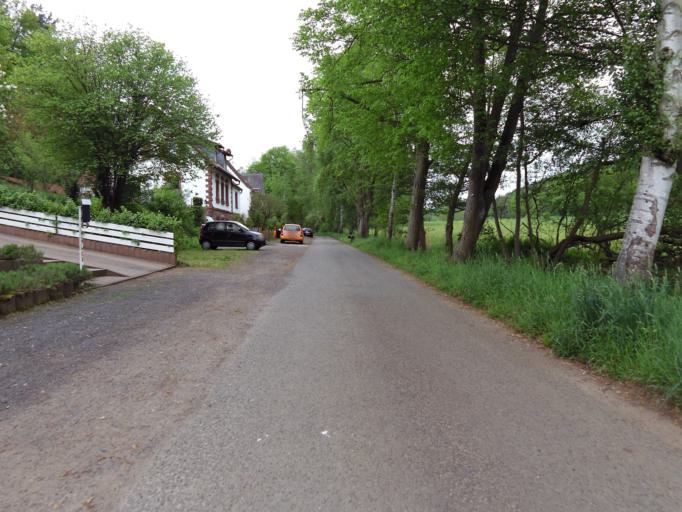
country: DE
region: Rheinland-Pfalz
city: Altleiningen
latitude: 49.5057
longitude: 8.0722
